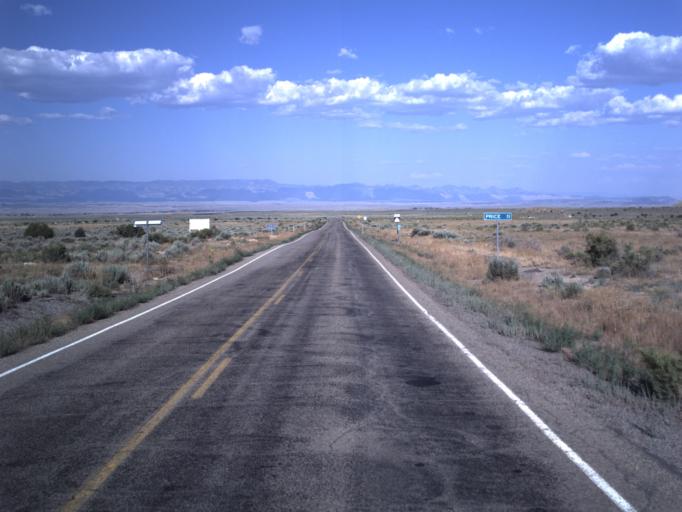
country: US
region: Utah
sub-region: Carbon County
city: Price
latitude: 39.4843
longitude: -110.8969
